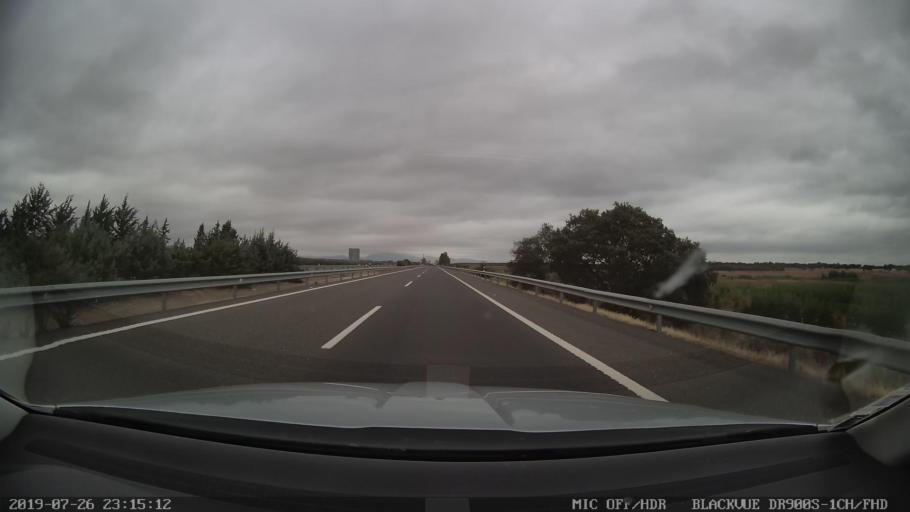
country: ES
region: Extremadura
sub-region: Provincia de Badajoz
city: Santa Amalia
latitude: 39.0501
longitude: -6.0585
